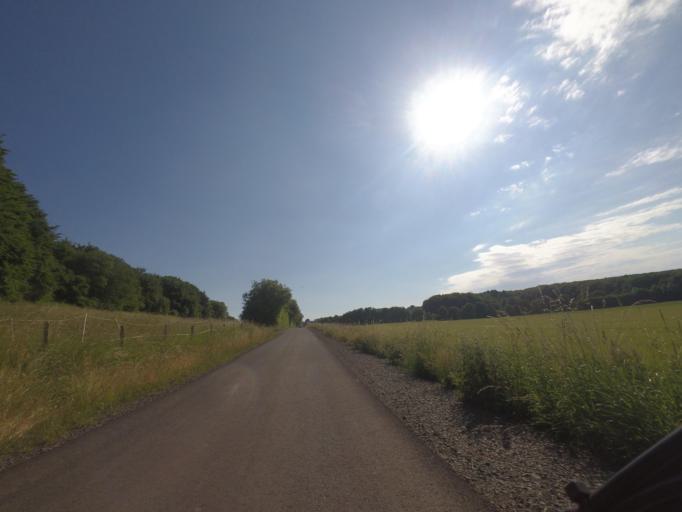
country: DE
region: Rheinland-Pfalz
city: Esch
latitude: 50.3711
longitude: 6.6201
